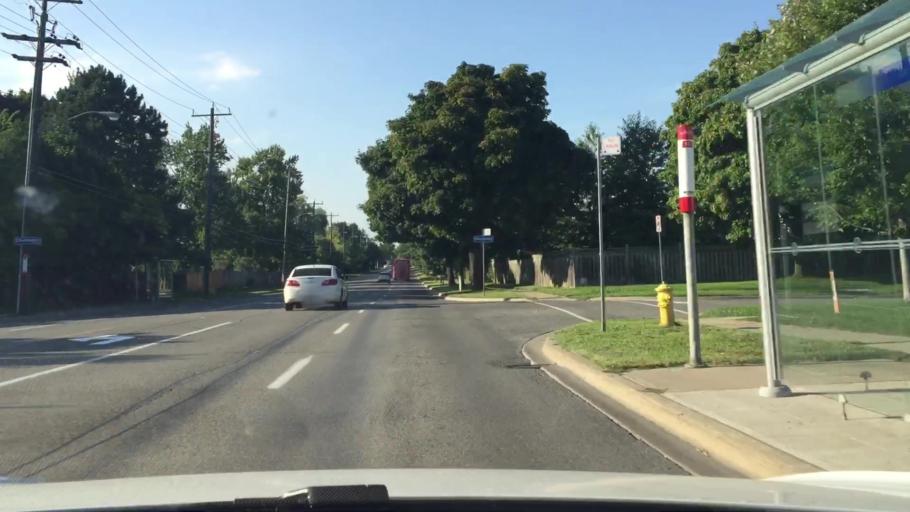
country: CA
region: Ontario
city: Scarborough
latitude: 43.7932
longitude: -79.3034
